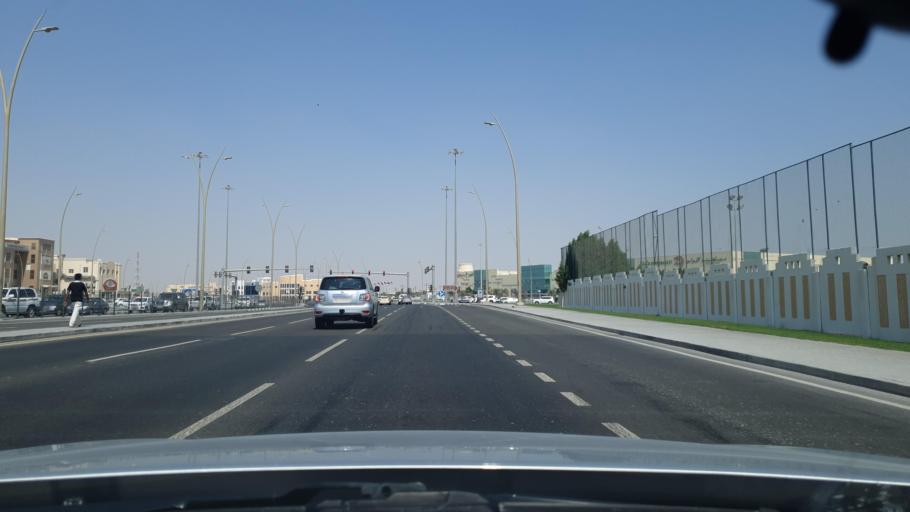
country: QA
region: Al Khawr
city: Al Khawr
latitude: 25.6724
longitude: 51.5011
